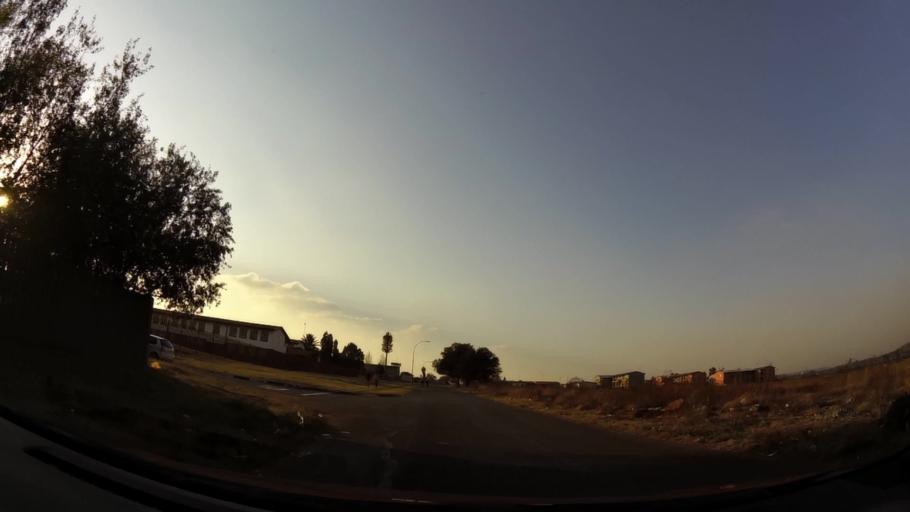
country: ZA
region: Gauteng
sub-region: City of Johannesburg Metropolitan Municipality
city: Soweto
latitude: -26.2862
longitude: 27.9053
